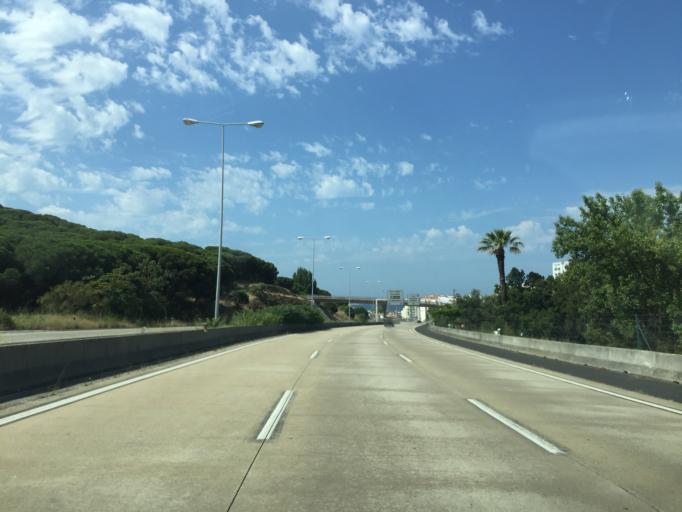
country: PT
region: Lisbon
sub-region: Oeiras
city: Alges
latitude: 38.7062
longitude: -9.2237
